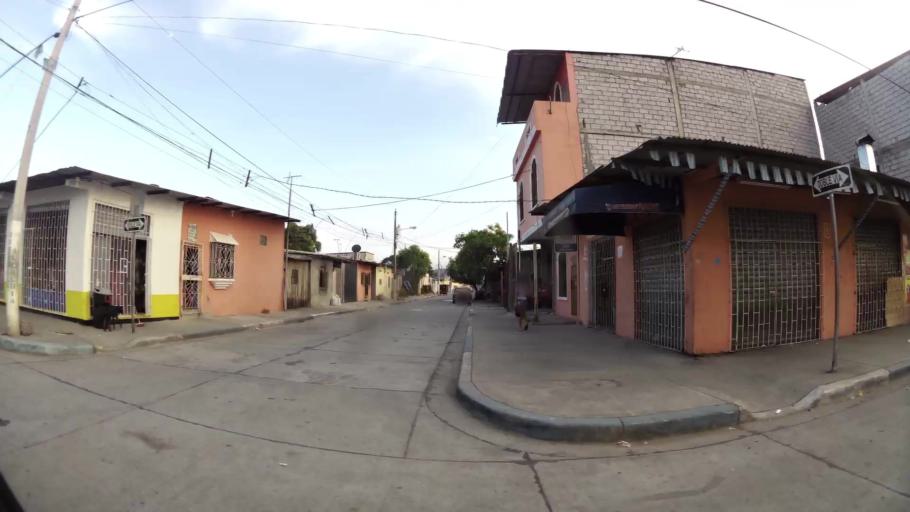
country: EC
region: Guayas
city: Eloy Alfaro
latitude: -2.0888
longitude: -79.8971
